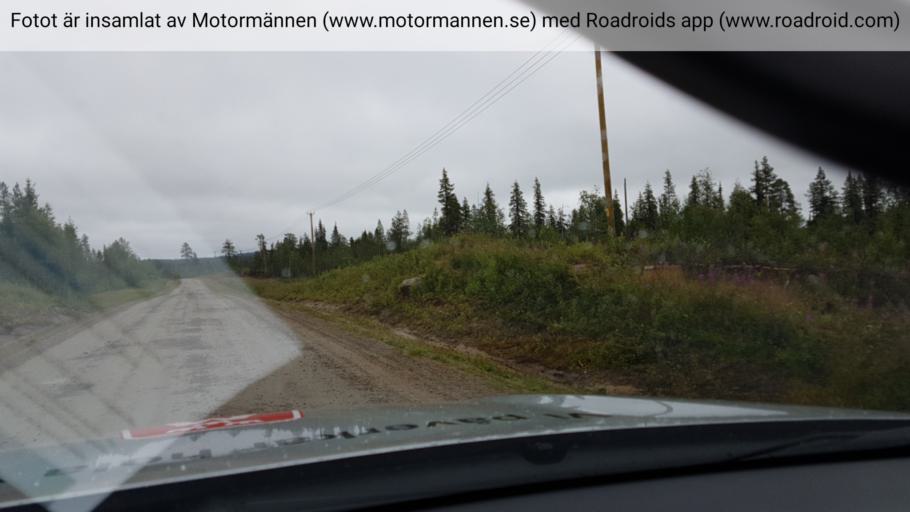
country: SE
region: Norrbotten
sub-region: Gallivare Kommun
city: Gaellivare
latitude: 66.7085
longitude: 20.4624
